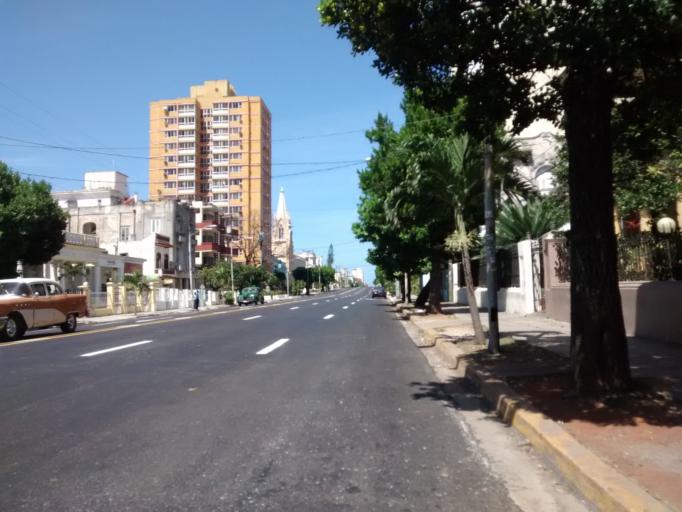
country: CU
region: La Habana
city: Havana
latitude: 23.1339
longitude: -82.3906
